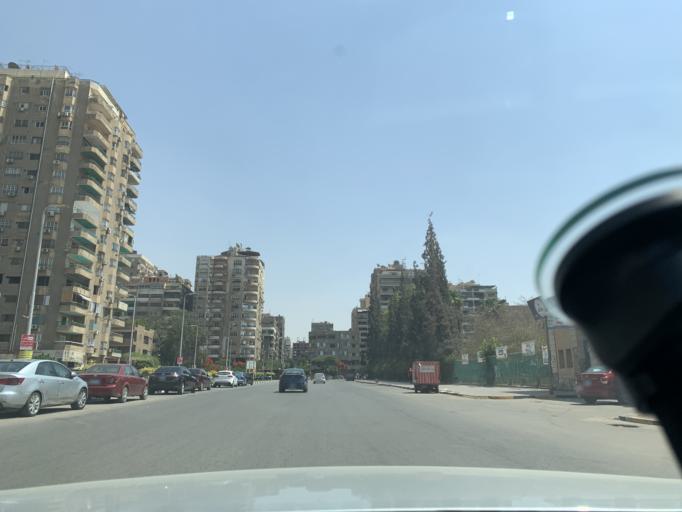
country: EG
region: Muhafazat al Qahirah
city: Cairo
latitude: 30.0623
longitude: 31.3495
